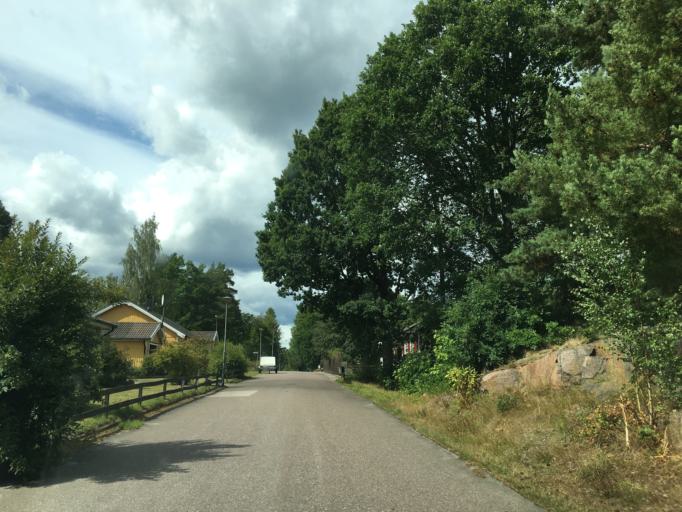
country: SE
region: Kalmar
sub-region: Nybro Kommun
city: Nybro
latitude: 56.9406
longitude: 15.9205
